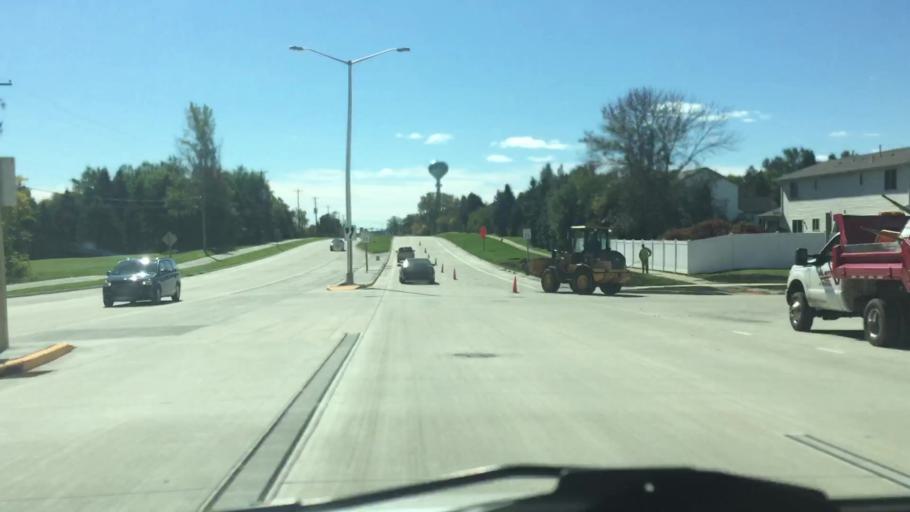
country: US
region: Wisconsin
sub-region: Waukesha County
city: Pewaukee
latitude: 43.0431
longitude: -88.2859
